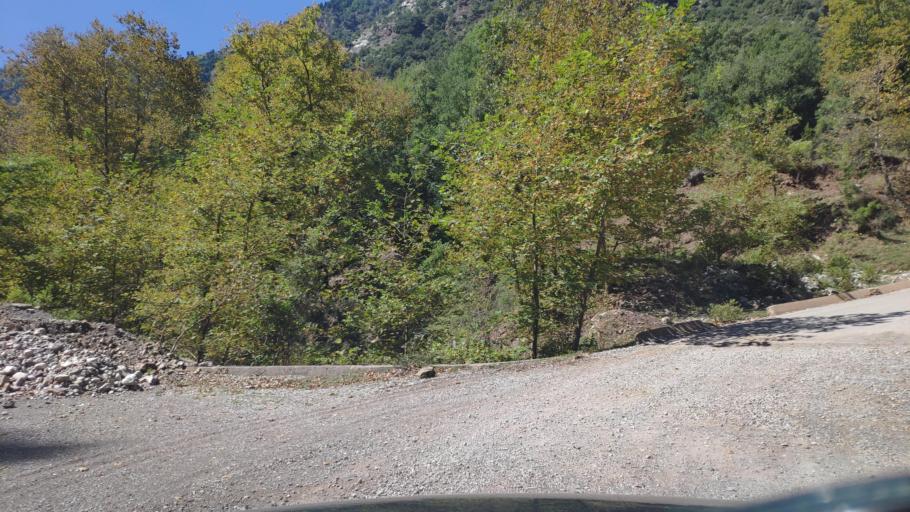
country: GR
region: Central Greece
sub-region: Nomos Evrytanias
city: Kerasochori
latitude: 39.0749
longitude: 21.5986
